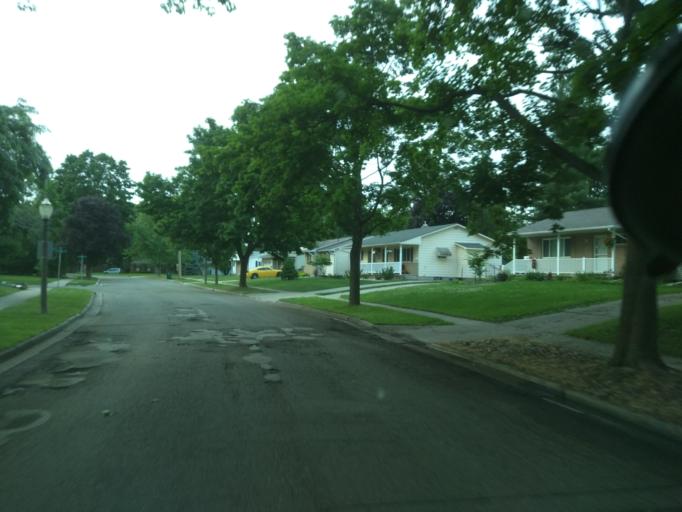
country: US
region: Michigan
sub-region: Ingham County
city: Lansing
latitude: 42.7029
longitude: -84.5737
